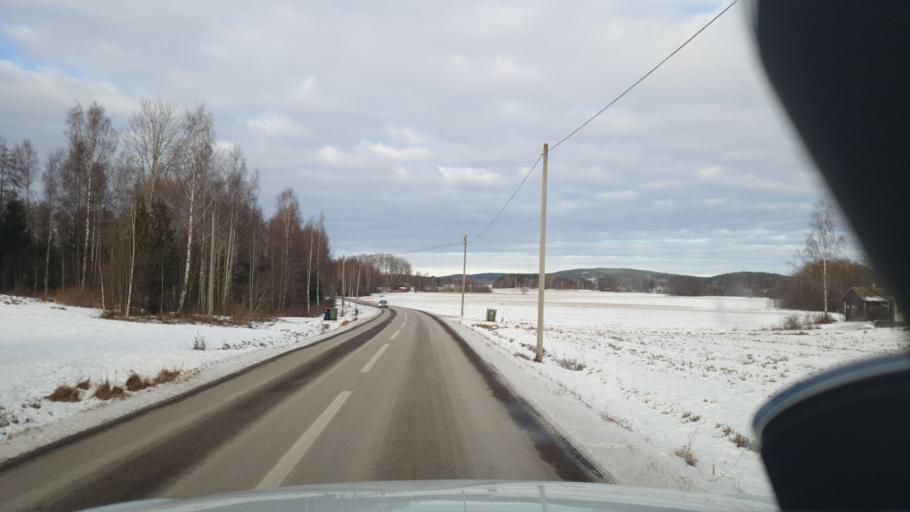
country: SE
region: Vaermland
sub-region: Arvika Kommun
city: Arvika
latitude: 59.6007
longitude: 12.5359
